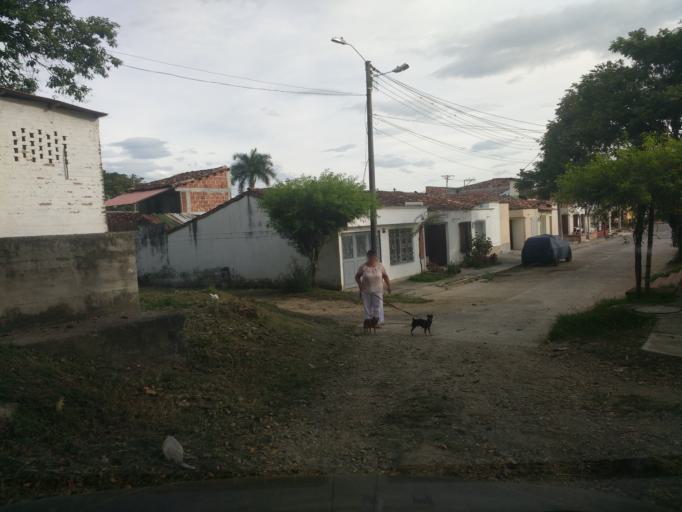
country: CO
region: Valle del Cauca
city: Cartago
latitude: 4.7621
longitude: -75.9250
